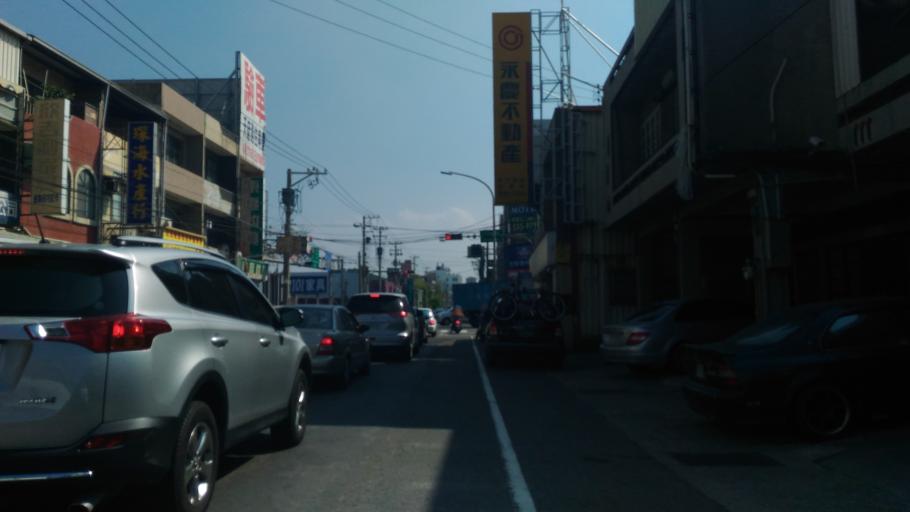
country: TW
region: Taiwan
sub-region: Hsinchu
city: Hsinchu
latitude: 24.8426
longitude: 120.9335
